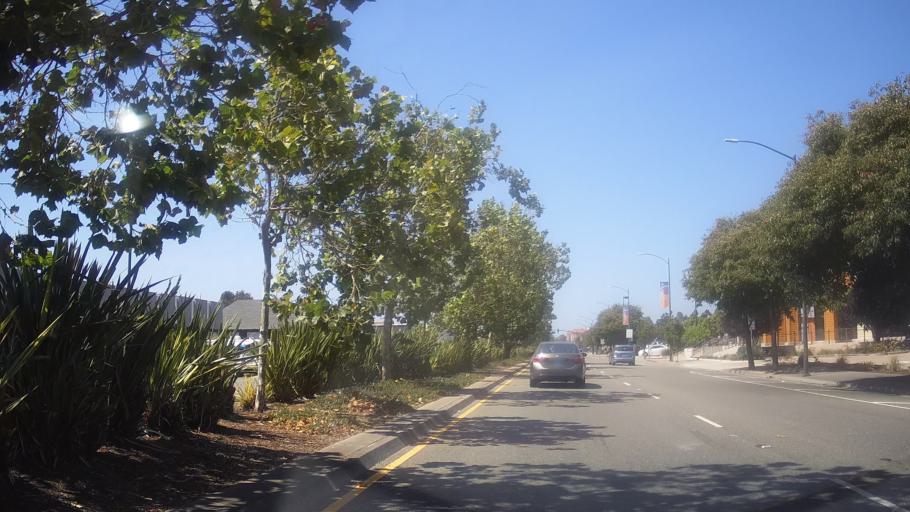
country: US
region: California
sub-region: Contra Costa County
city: El Cerrito
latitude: 37.9218
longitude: -122.3159
